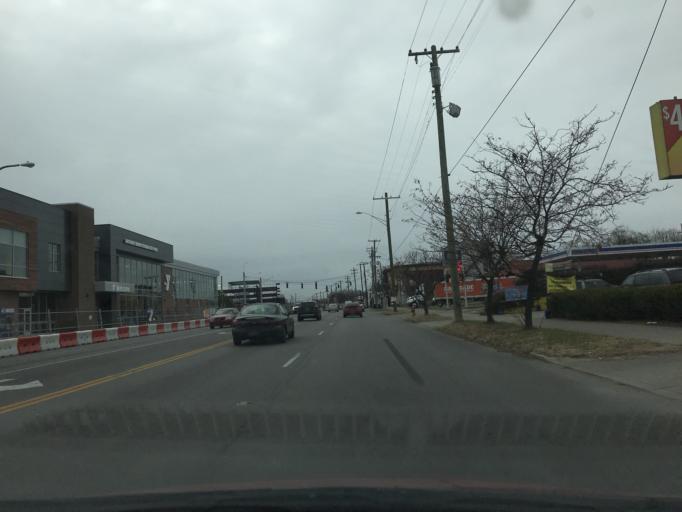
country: US
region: Kentucky
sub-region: Jefferson County
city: Louisville
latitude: 38.2488
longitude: -85.7800
